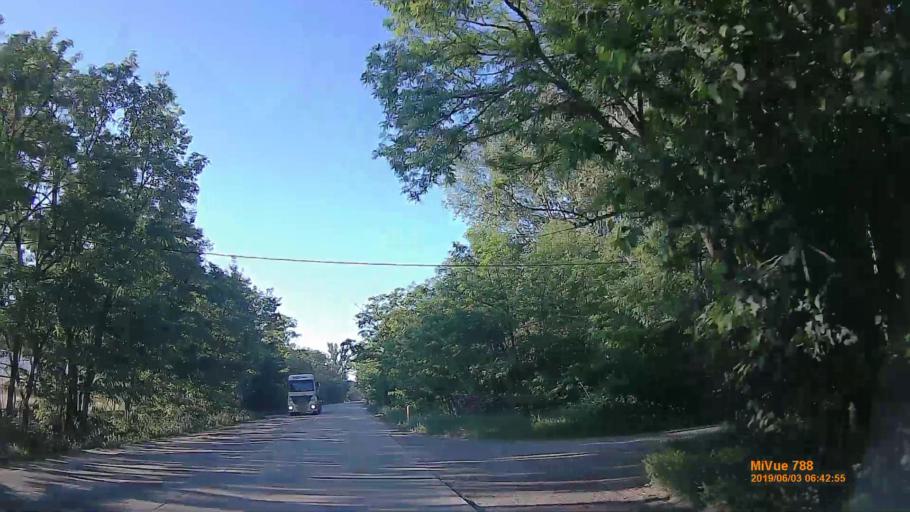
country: HU
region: Pest
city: Delegyhaza
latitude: 47.2611
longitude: 19.1202
